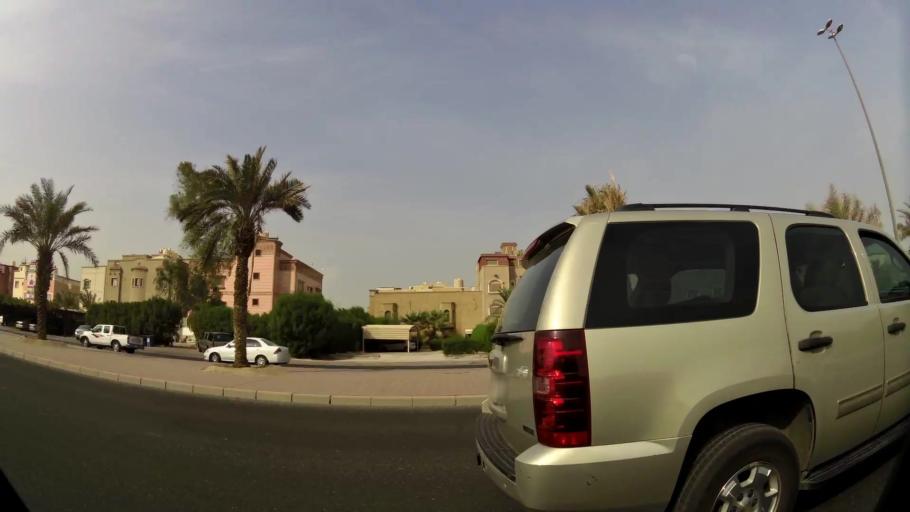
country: KW
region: Al Asimah
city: Ar Rabiyah
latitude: 29.2800
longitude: 47.9407
